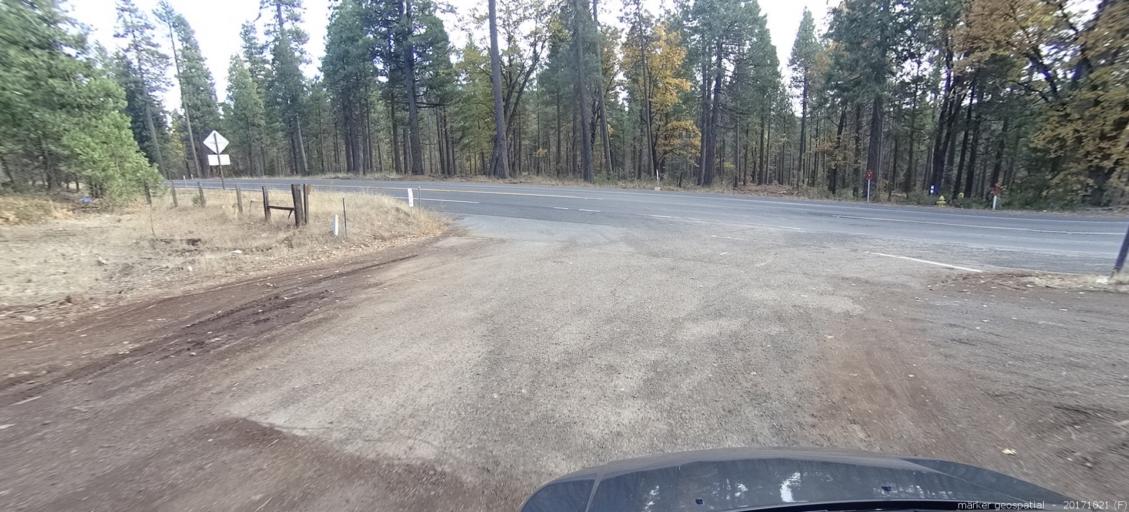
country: US
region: California
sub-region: Shasta County
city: Burney
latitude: 40.8727
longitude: -121.6947
